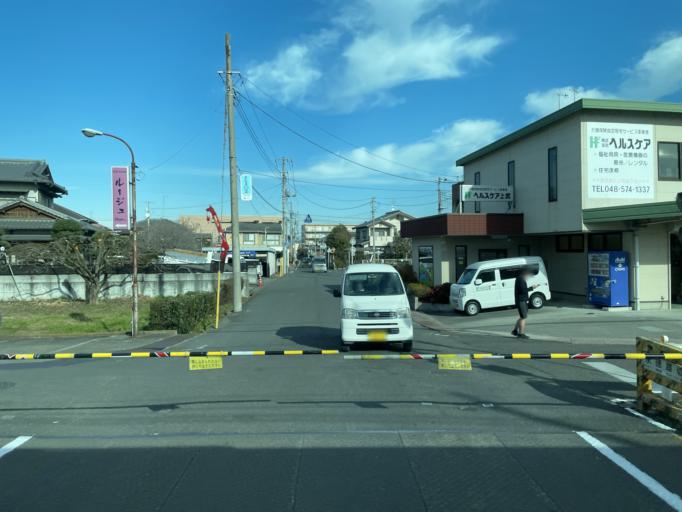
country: JP
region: Saitama
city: Fukayacho
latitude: 36.1899
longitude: 139.2879
